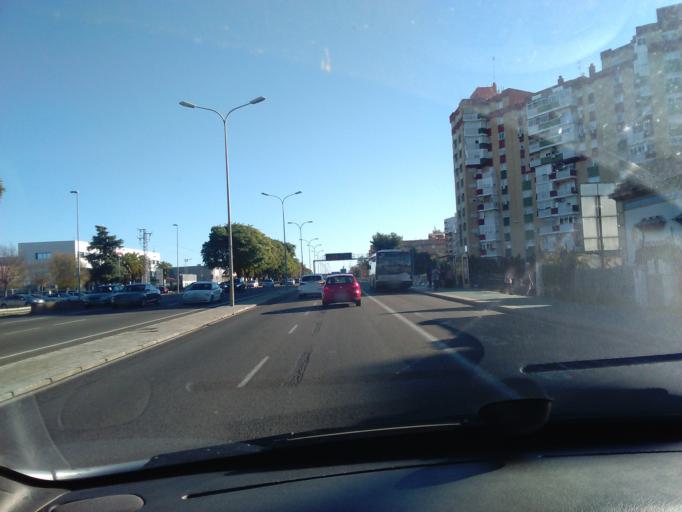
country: ES
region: Andalusia
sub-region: Provincia de Sevilla
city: Sevilla
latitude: 37.3866
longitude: -5.9471
